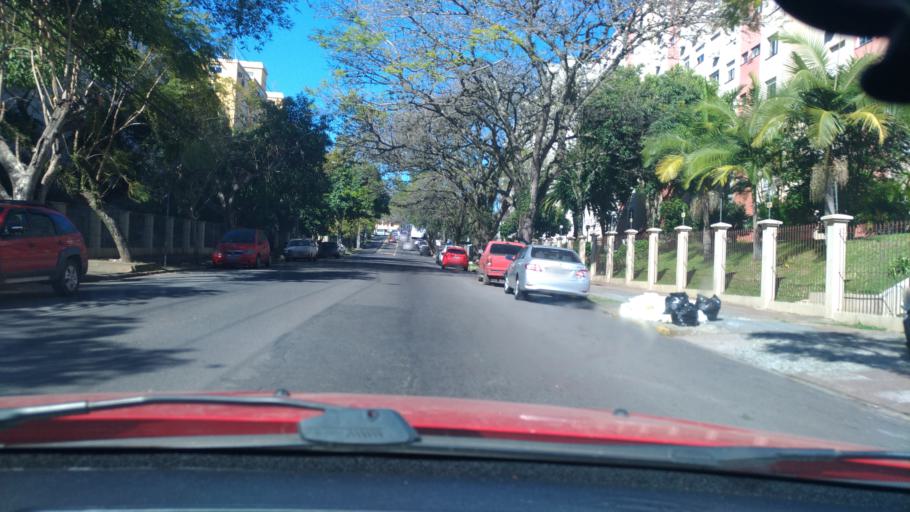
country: BR
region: Rio Grande do Sul
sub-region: Porto Alegre
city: Porto Alegre
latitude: -30.0409
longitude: -51.1452
